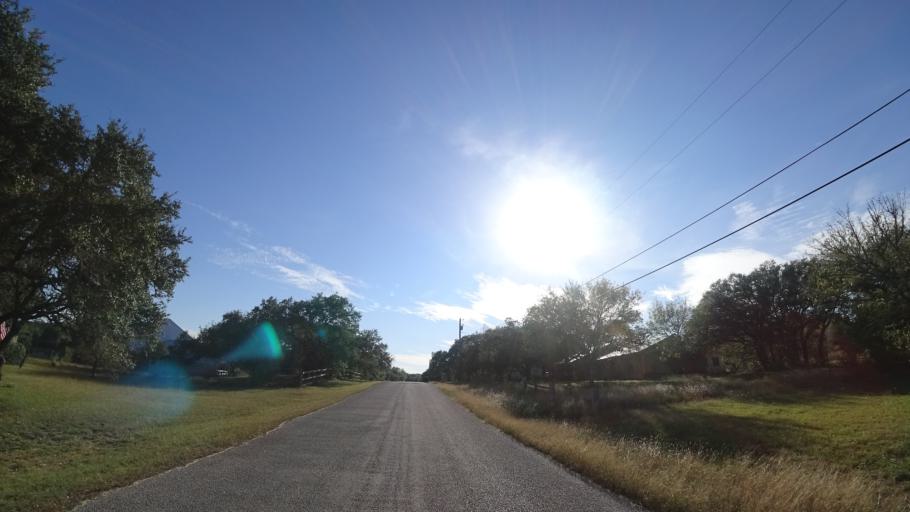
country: US
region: Texas
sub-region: Travis County
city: Barton Creek
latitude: 30.2449
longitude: -97.9140
